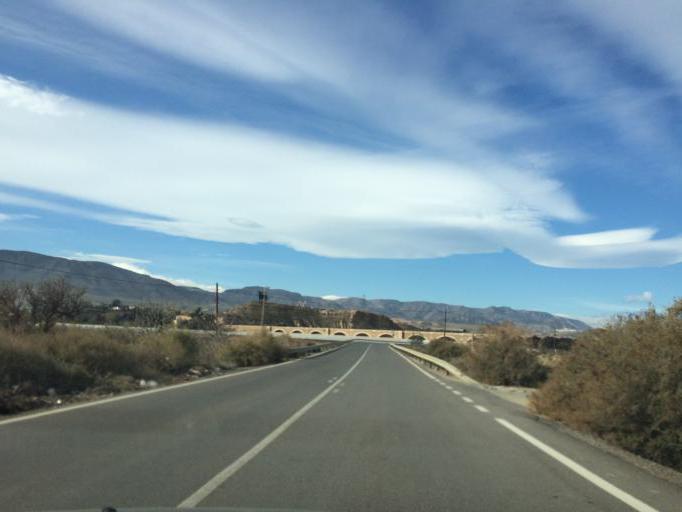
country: ES
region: Andalusia
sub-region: Provincia de Almeria
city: Rioja
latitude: 36.9381
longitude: -2.4545
